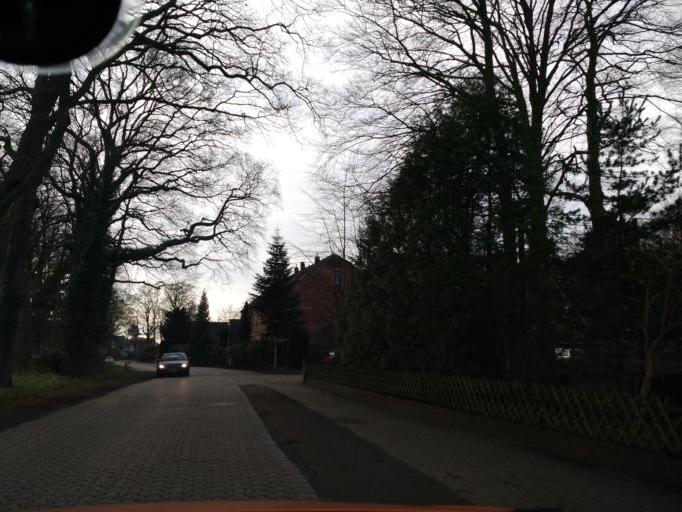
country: DE
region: Lower Saxony
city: Hude
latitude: 53.1038
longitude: 8.4679
